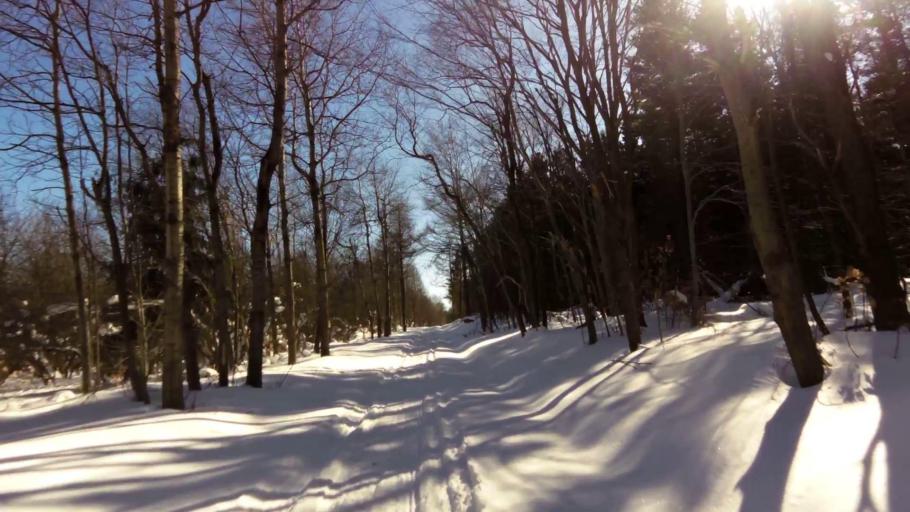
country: US
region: New York
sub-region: Cattaraugus County
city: Franklinville
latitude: 42.3432
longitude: -78.3591
